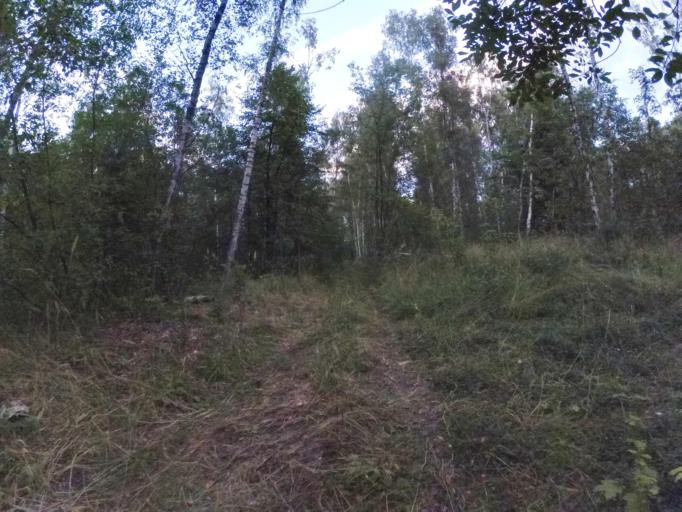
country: RU
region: Moskovskaya
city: Kotel'niki
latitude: 55.6646
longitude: 37.8205
